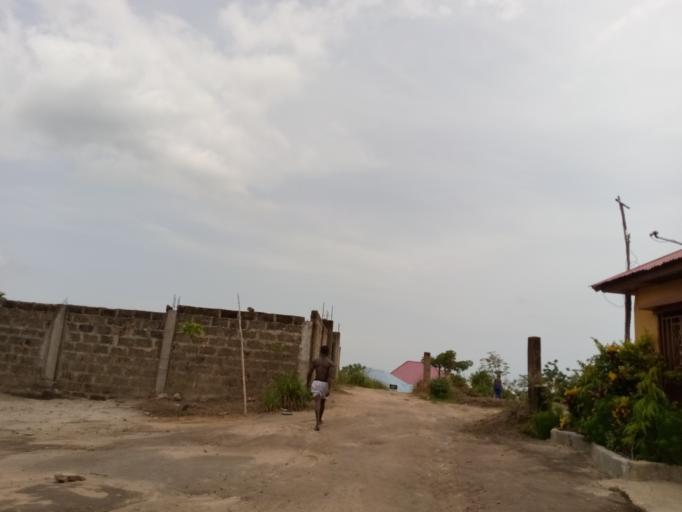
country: SL
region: Western Area
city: Waterloo
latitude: 8.3321
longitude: -13.0276
